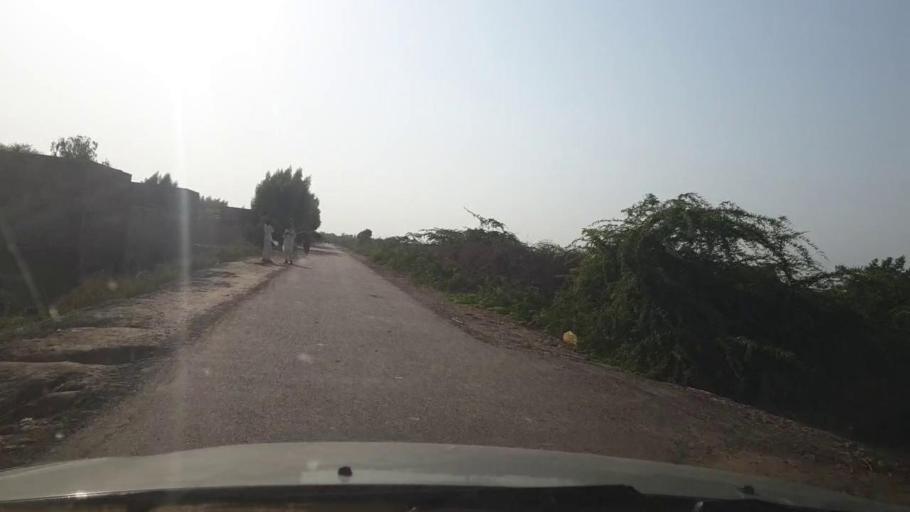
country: PK
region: Sindh
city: Tando Ghulam Ali
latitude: 25.1834
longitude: 68.9457
